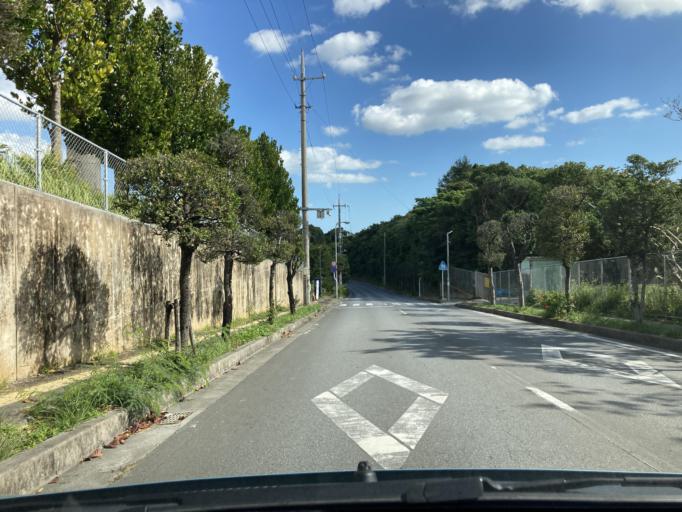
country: JP
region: Okinawa
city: Okinawa
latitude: 26.3431
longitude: 127.8006
